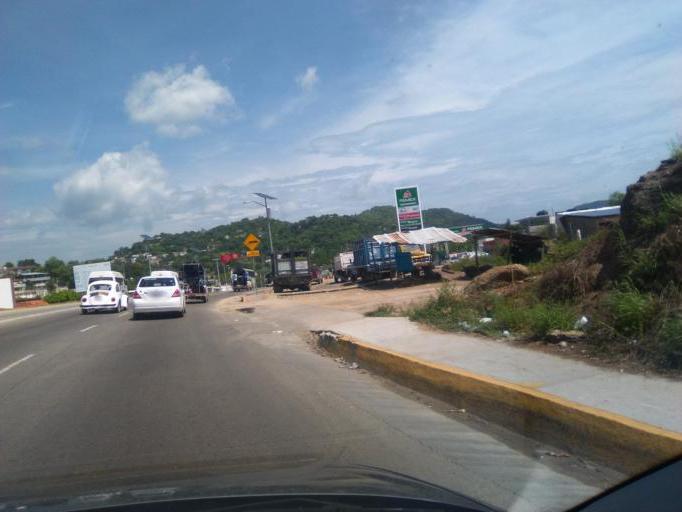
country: MX
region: Guerrero
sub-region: Acapulco de Juarez
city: Colonia Nueva Revolucion
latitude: 16.9102
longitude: -99.8238
